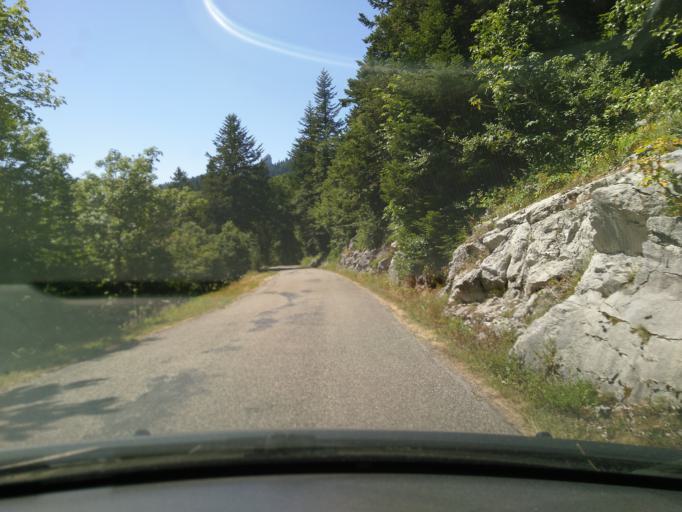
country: FR
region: Rhone-Alpes
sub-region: Departement de l'Isere
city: Le Sappey-en-Chartreuse
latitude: 45.3077
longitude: 5.7546
